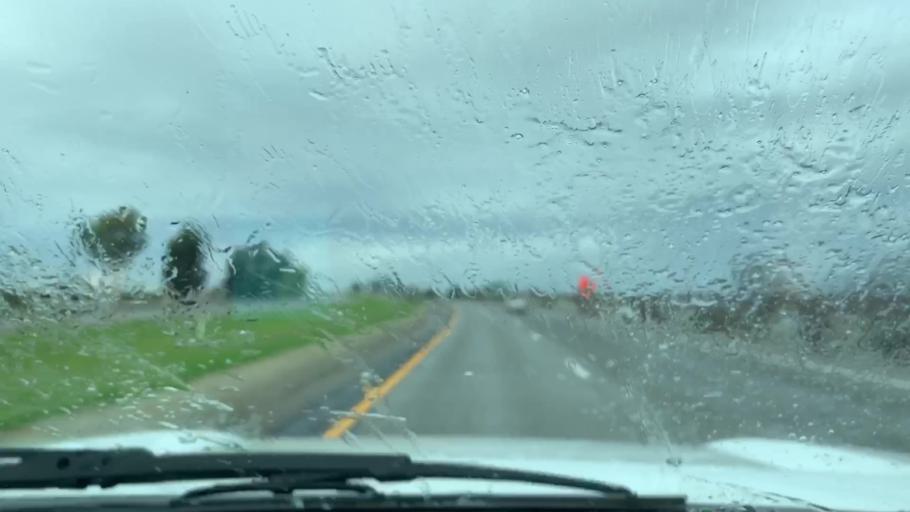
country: US
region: California
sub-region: Kings County
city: Lemoore
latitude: 36.2879
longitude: -119.8079
